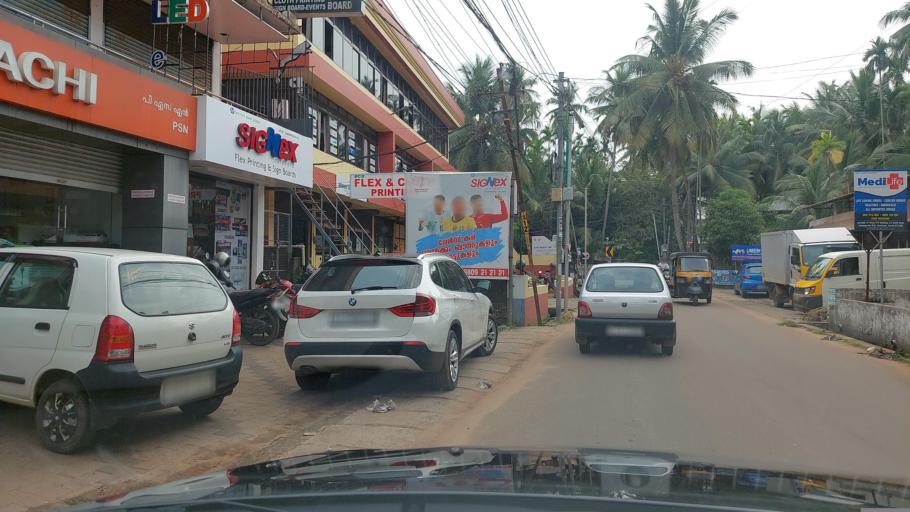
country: IN
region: Kerala
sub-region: Kozhikode
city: Kozhikode
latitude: 11.2500
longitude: 75.7883
